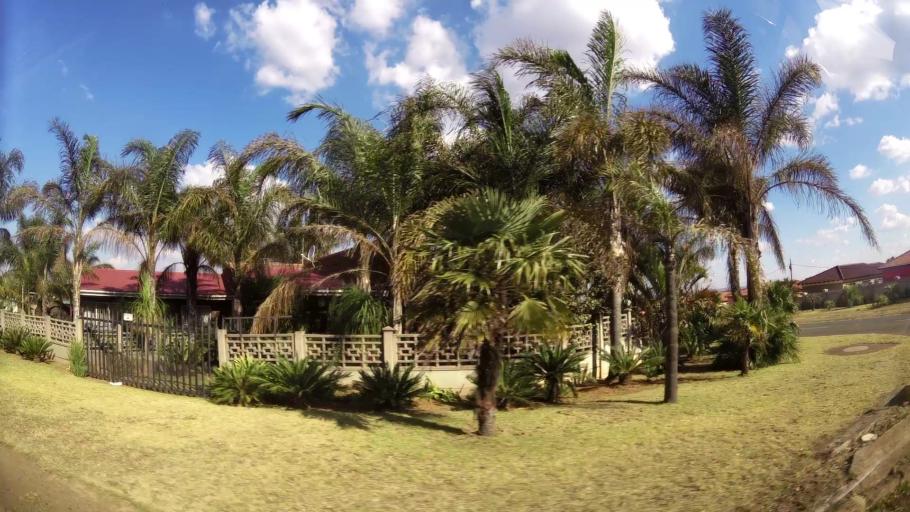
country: ZA
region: Mpumalanga
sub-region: Nkangala District Municipality
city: Witbank
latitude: -25.9085
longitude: 29.2297
